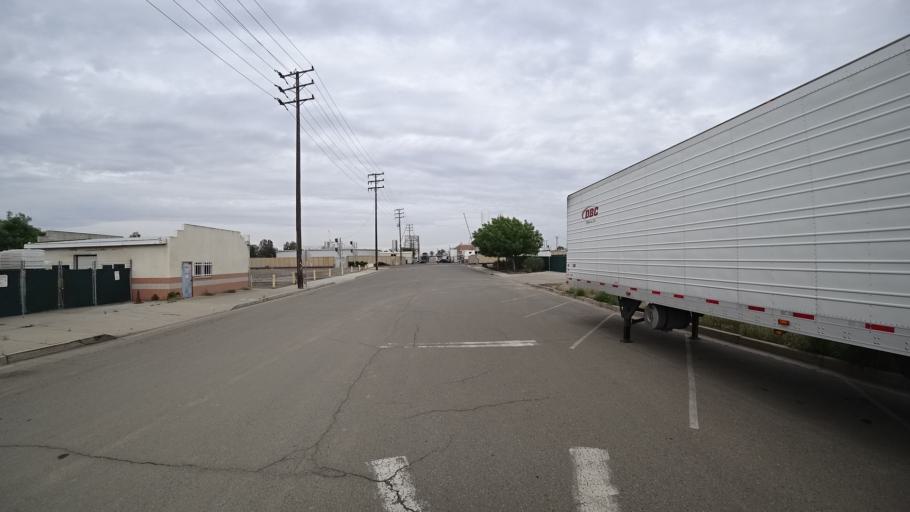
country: US
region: California
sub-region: Kings County
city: Hanford
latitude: 36.3239
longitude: -119.6506
